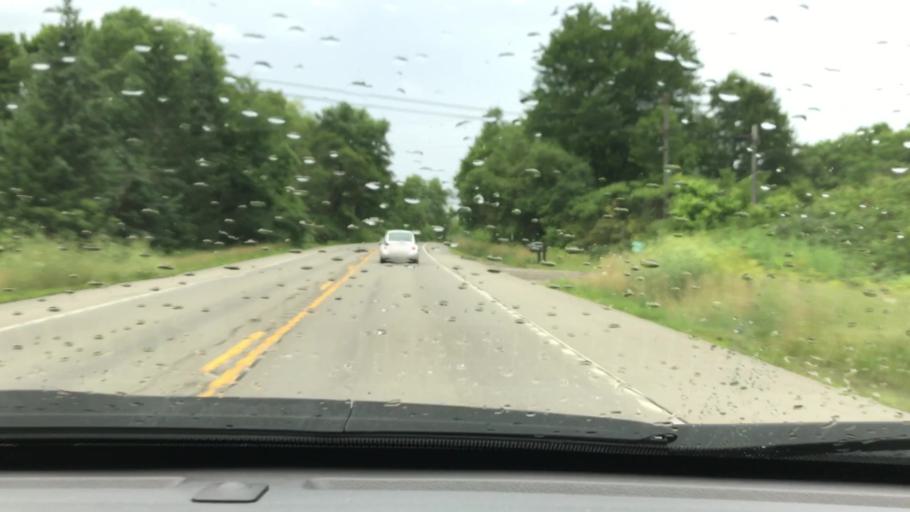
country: US
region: New York
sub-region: Cattaraugus County
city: Salamanca
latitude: 42.1873
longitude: -78.6784
